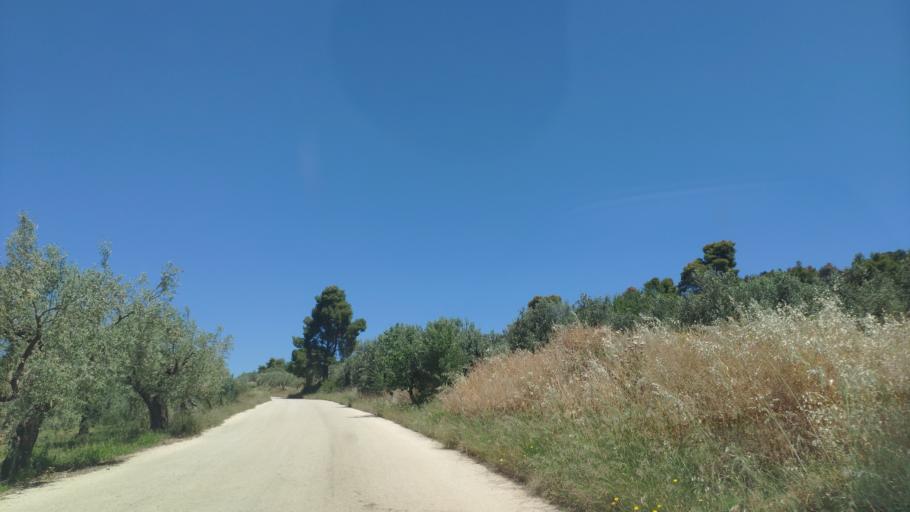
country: GR
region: Peloponnese
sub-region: Nomos Korinthias
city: Athikia
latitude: 37.8289
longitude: 22.9287
